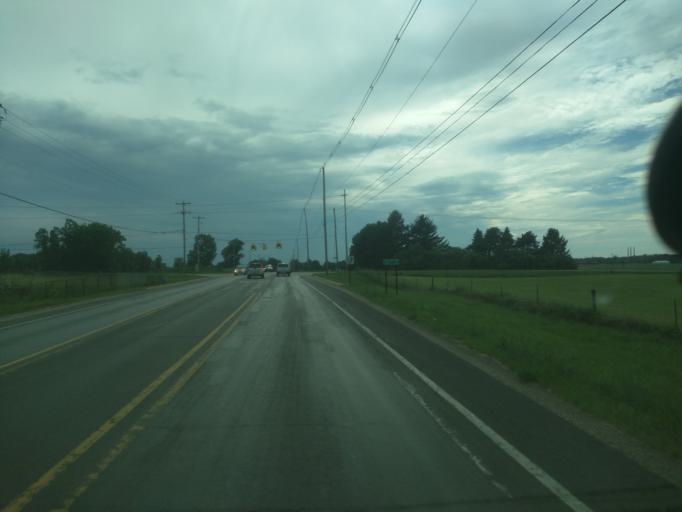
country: US
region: Michigan
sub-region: Ingham County
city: Holt
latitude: 42.6828
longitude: -84.4828
